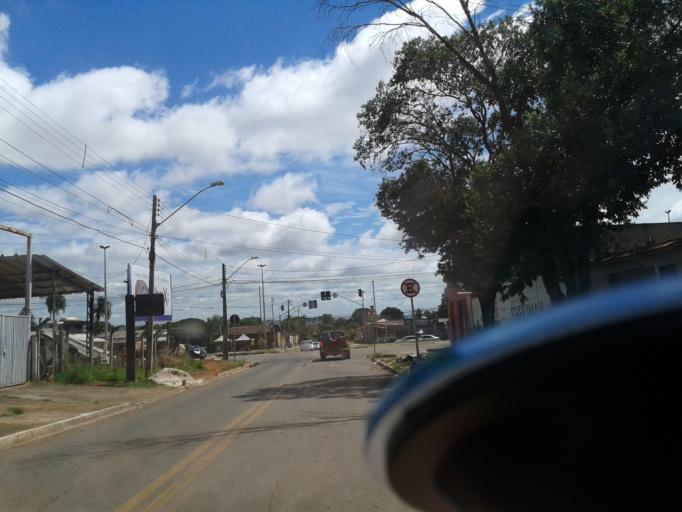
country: BR
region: Goias
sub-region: Goiania
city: Goiania
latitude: -16.6501
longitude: -49.3354
